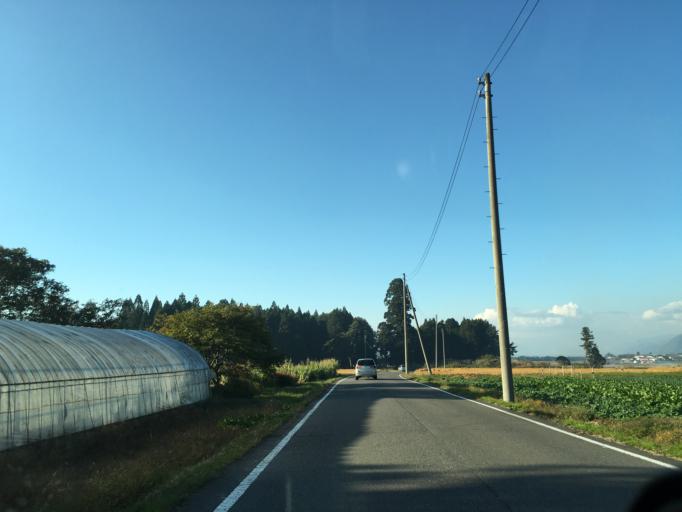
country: JP
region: Fukushima
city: Inawashiro
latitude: 37.4096
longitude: 140.1446
